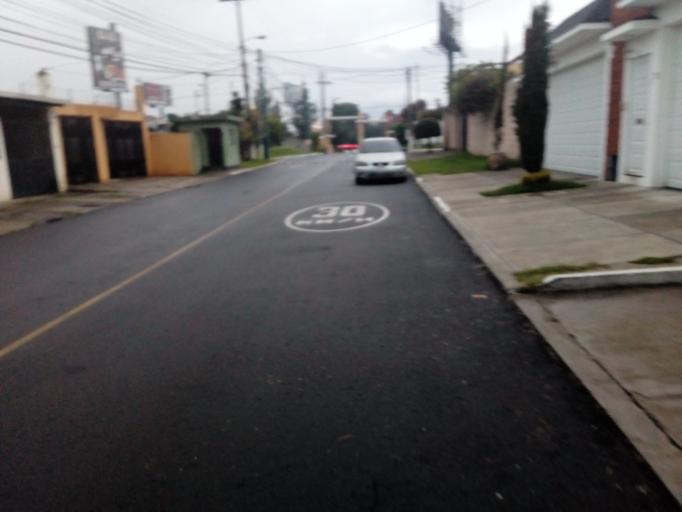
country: GT
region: Guatemala
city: Mixco
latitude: 14.5998
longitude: -90.5781
